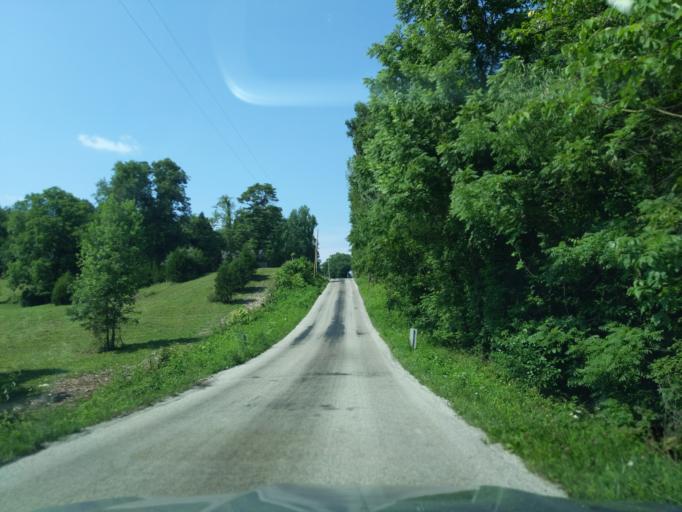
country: US
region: Indiana
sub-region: Ripley County
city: Osgood
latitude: 39.1075
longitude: -85.3441
